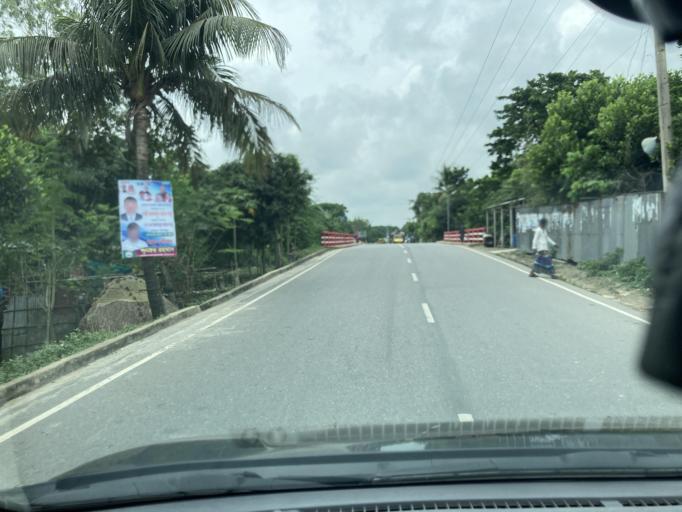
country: BD
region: Dhaka
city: Azimpur
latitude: 23.8058
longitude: 90.2114
